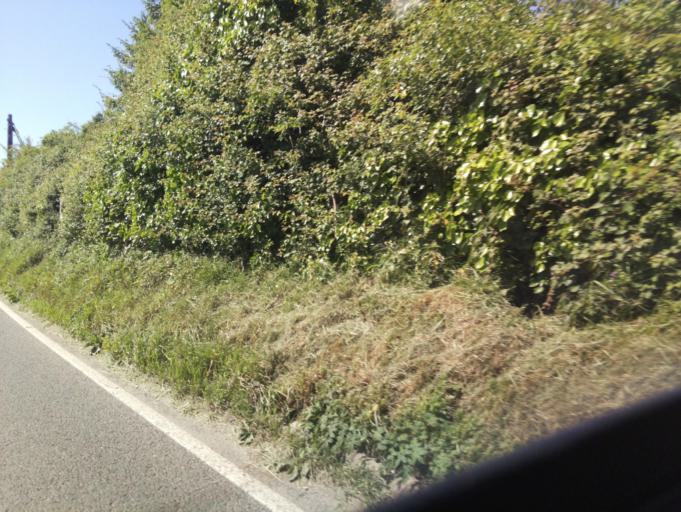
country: GB
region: England
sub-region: Somerset
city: Chard
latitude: 50.8761
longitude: -2.9863
